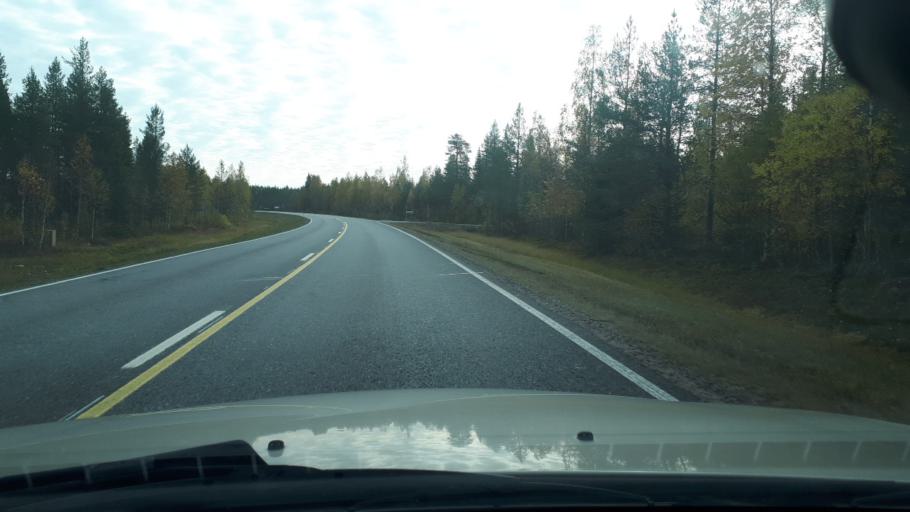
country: FI
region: Lapland
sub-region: Rovaniemi
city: Ranua
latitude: 65.9817
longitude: 26.3602
